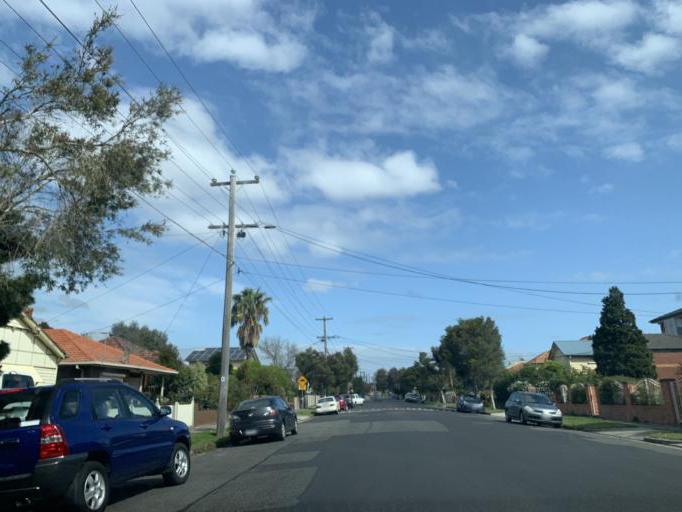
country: AU
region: Victoria
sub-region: Moreland
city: Coburg
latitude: -37.7432
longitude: 144.9739
